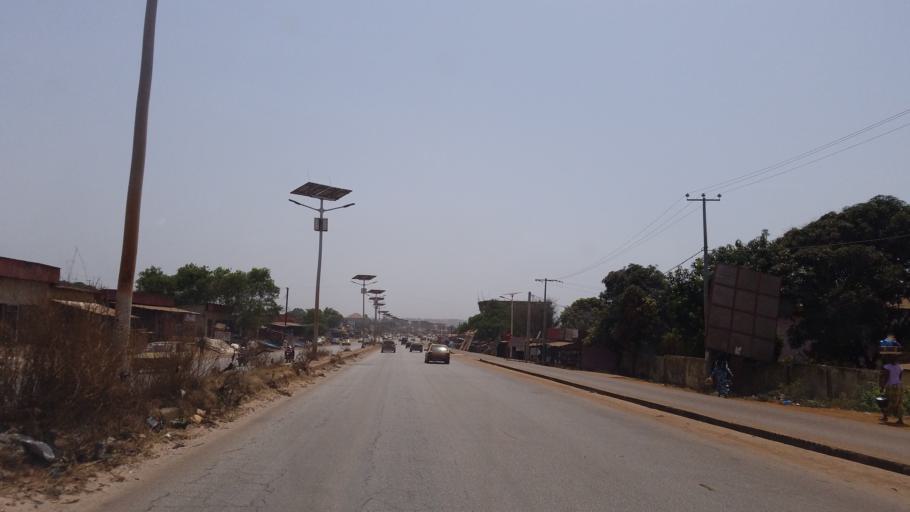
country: GN
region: Kindia
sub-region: Prefecture de Dubreka
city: Dubreka
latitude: 9.6613
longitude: -13.5650
